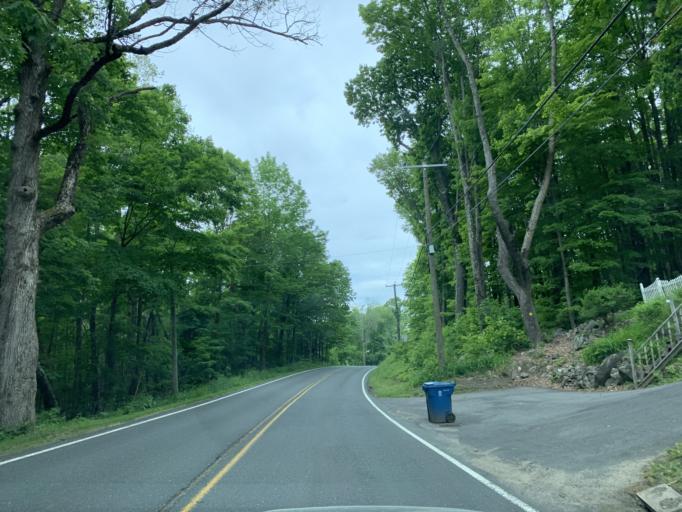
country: US
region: Massachusetts
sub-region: Hampshire County
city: Southampton
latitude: 42.2114
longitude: -72.8154
